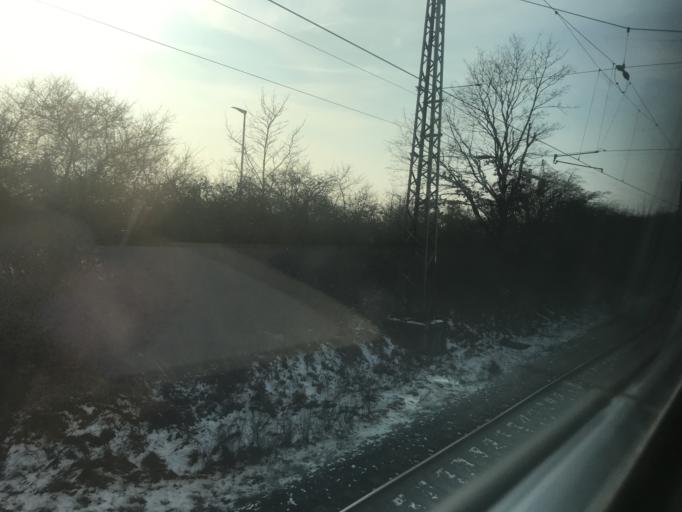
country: DE
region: Rheinland-Pfalz
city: Neuerburg
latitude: 49.9760
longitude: 6.9554
